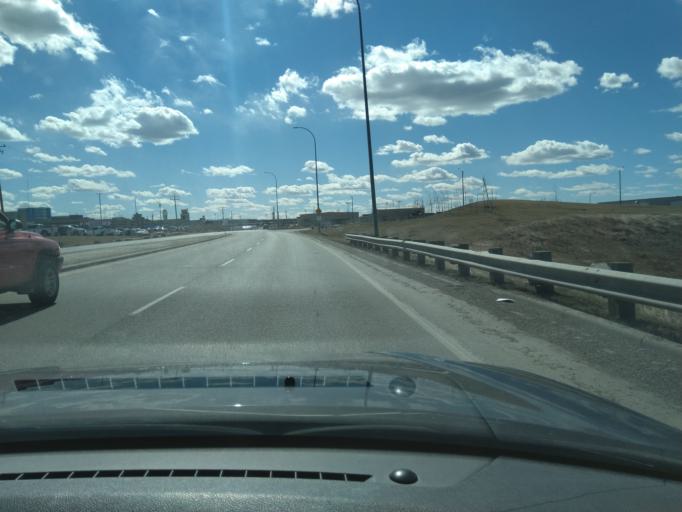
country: CA
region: Alberta
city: Calgary
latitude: 51.1387
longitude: -114.0135
